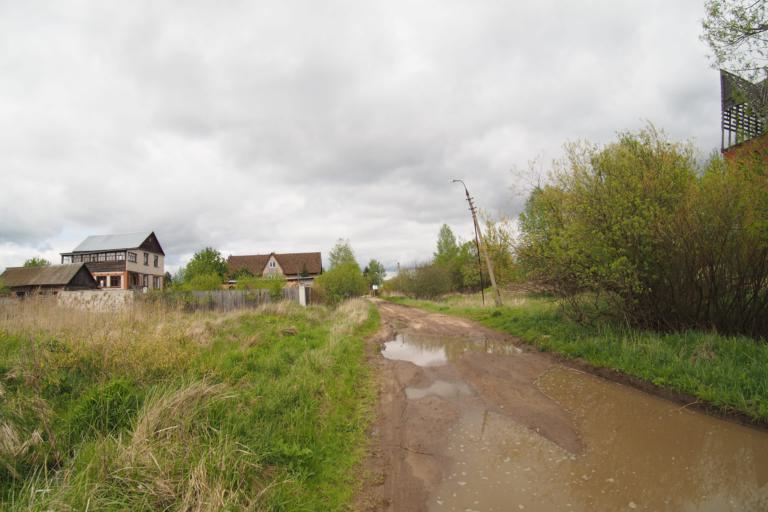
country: RU
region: Moskovskaya
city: Rechitsy
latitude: 55.5705
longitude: 38.4841
